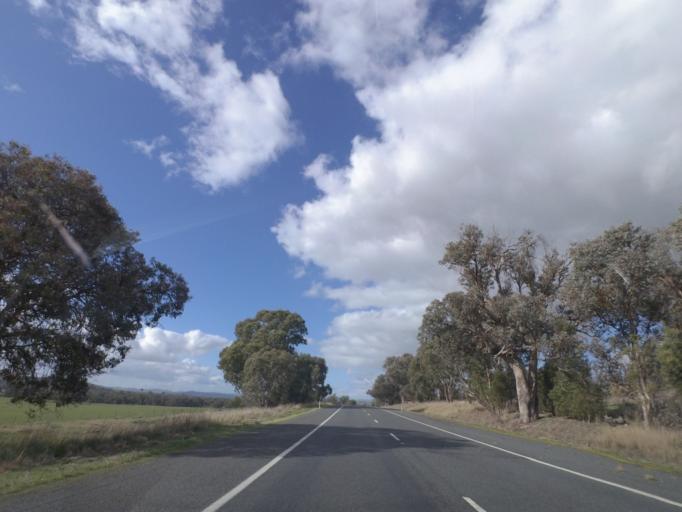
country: AU
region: New South Wales
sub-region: Greater Hume Shire
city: Holbrook
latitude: -35.6721
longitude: 147.3996
